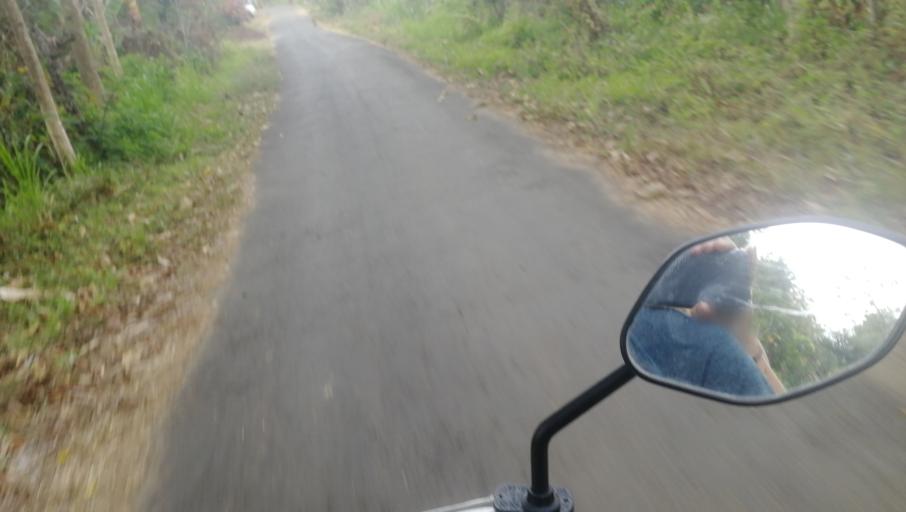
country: ID
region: Bali
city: Banjar Ambengan
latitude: -8.2126
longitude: 115.1099
